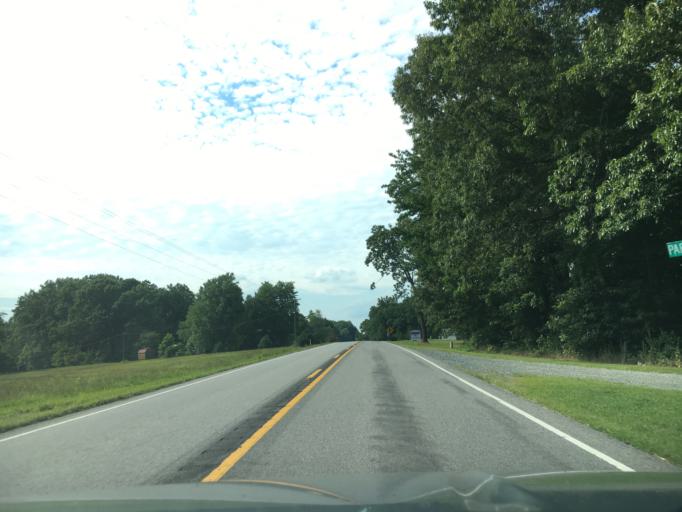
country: US
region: Virginia
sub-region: Halifax County
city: Mountain Road
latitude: 36.8675
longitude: -79.0109
